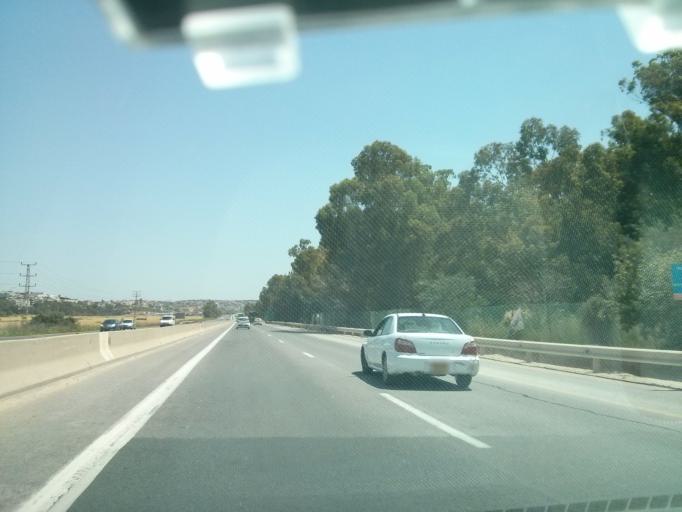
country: PS
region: West Bank
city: Barta`ah ash Sharqiyah
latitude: 32.4872
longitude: 35.0479
